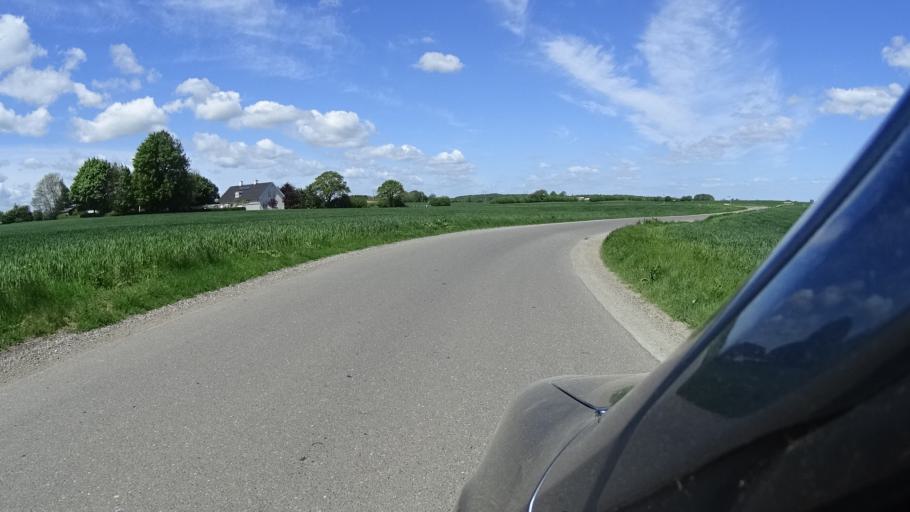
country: DK
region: South Denmark
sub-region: Vejle Kommune
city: Borkop
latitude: 55.6184
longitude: 9.6012
